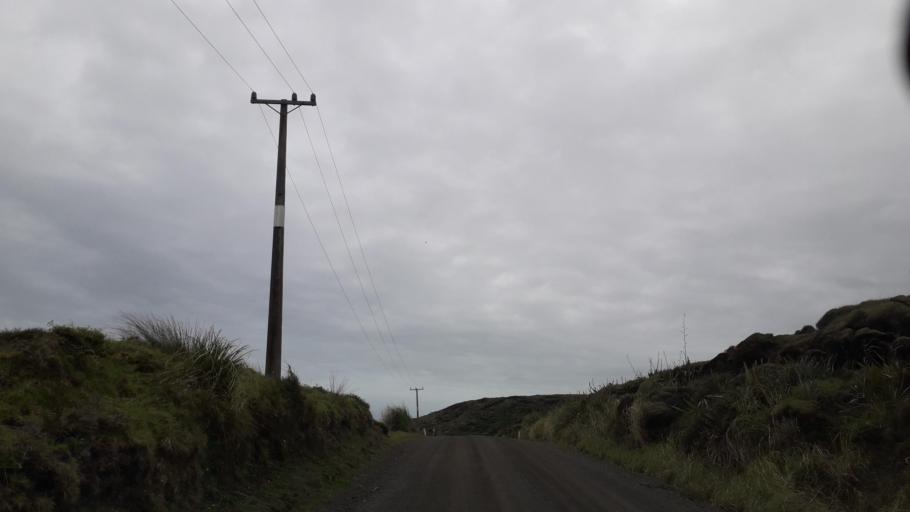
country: NZ
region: Northland
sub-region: Far North District
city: Ahipara
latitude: -35.4322
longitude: 173.2788
